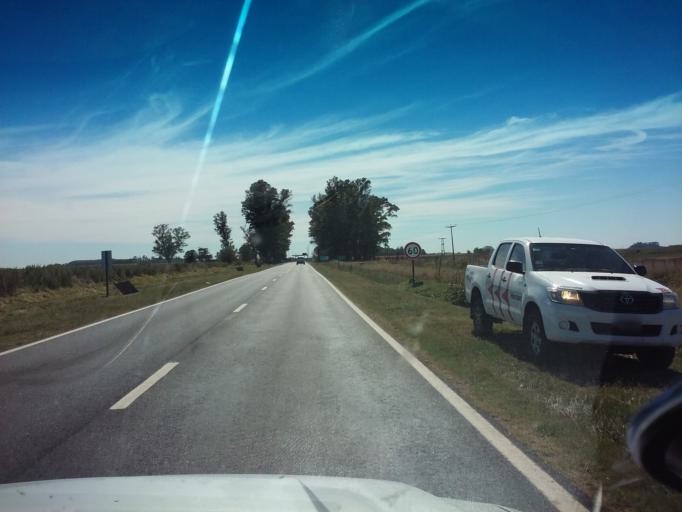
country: AR
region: Buenos Aires
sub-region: Partido de Nueve de Julio
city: Nueve de Julio
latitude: -35.3650
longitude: -60.7083
